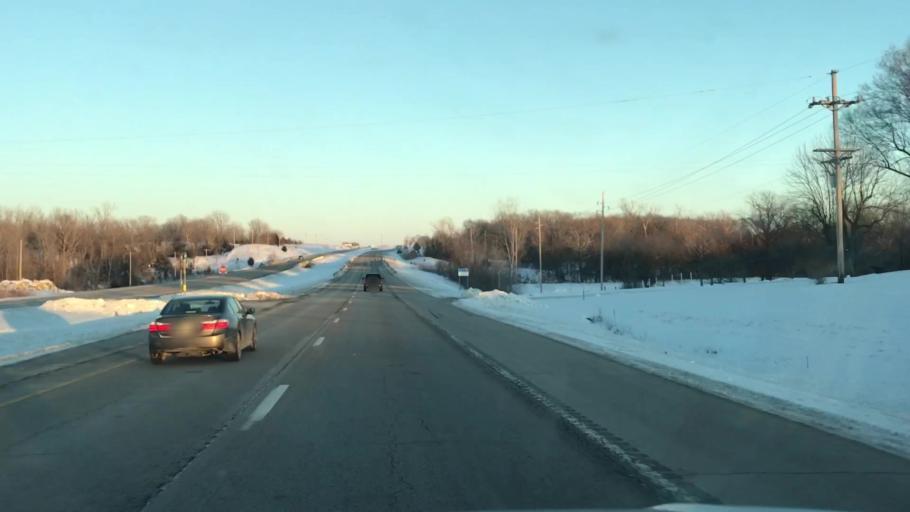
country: US
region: Missouri
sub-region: Clinton County
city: Cameron
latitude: 39.7547
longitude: -94.3196
